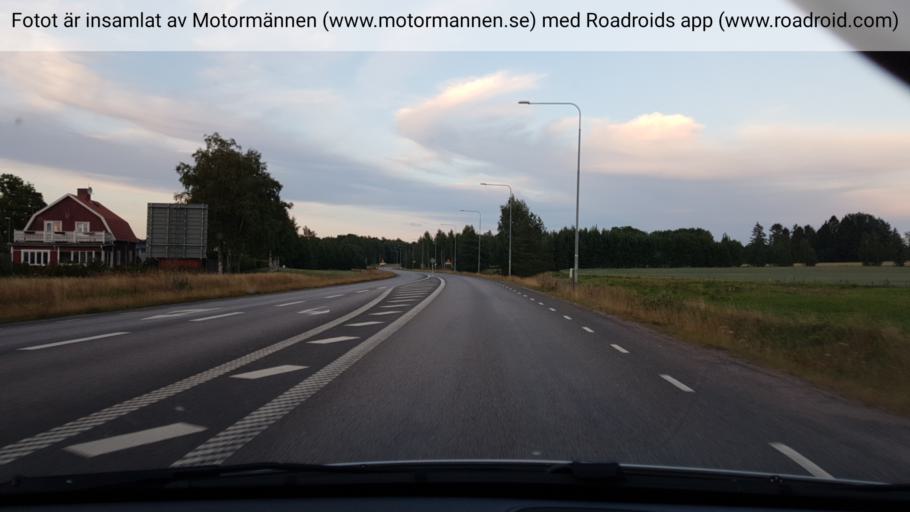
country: SE
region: Vaestra Goetaland
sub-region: Tibro Kommun
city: Tibro
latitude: 58.4138
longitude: 14.1553
